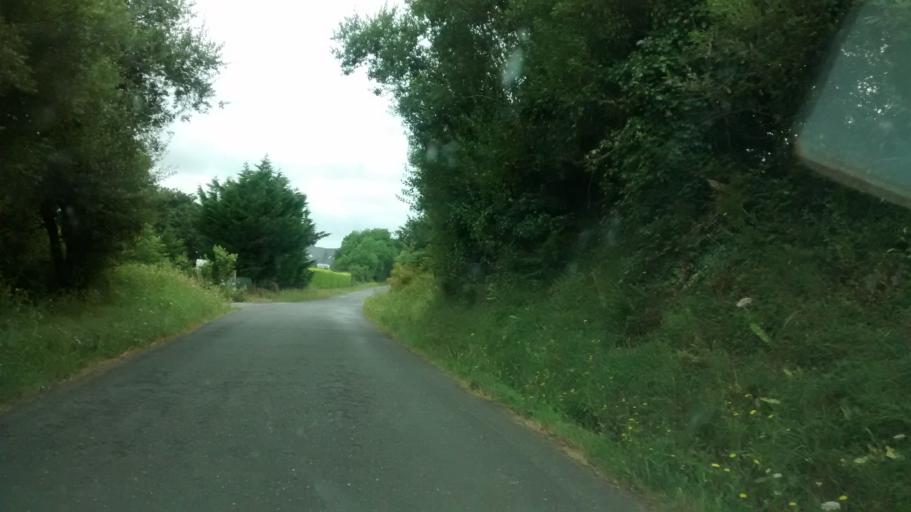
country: FR
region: Brittany
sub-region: Departement du Finistere
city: Lanveoc
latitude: 48.3303
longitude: -4.4417
